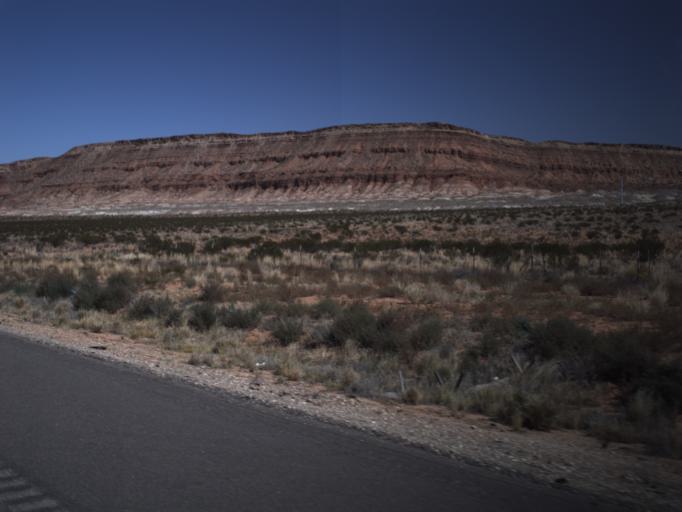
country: US
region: Utah
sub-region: Washington County
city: Washington
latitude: 37.0303
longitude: -113.4852
